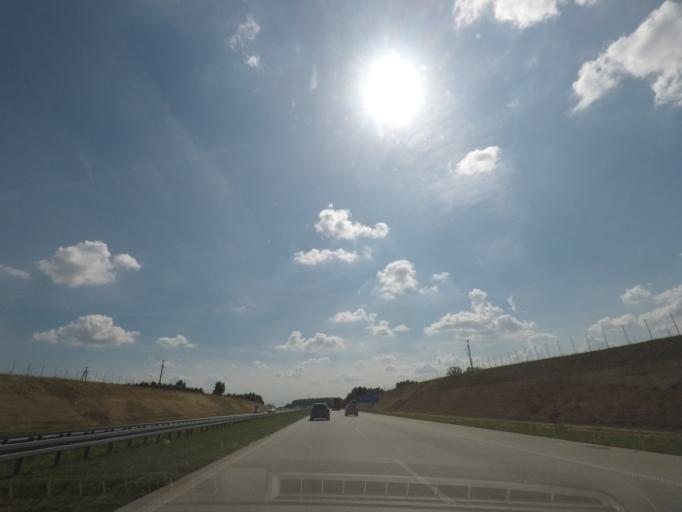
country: PL
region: Lodz Voivodeship
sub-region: Powiat lodzki wschodni
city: Andrespol
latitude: 51.7777
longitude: 19.6060
